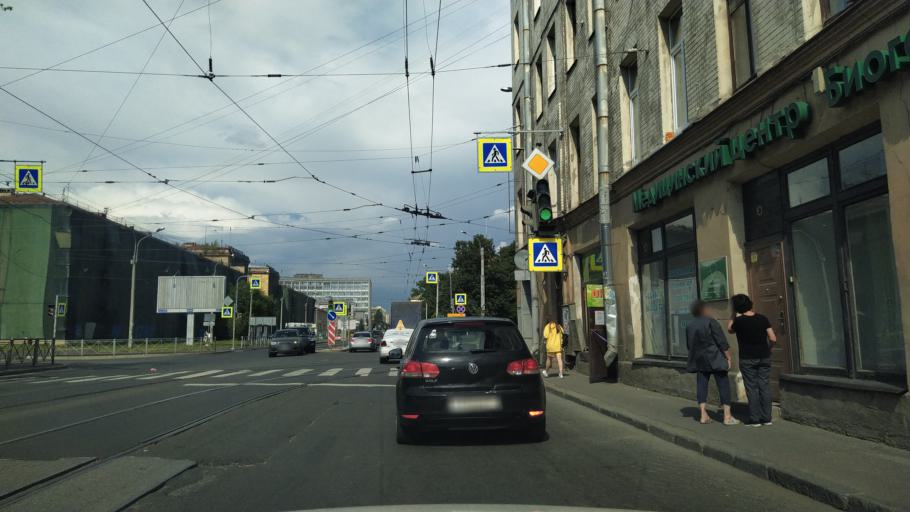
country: RU
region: Leningrad
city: Finlyandskiy
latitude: 59.9674
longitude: 30.3839
